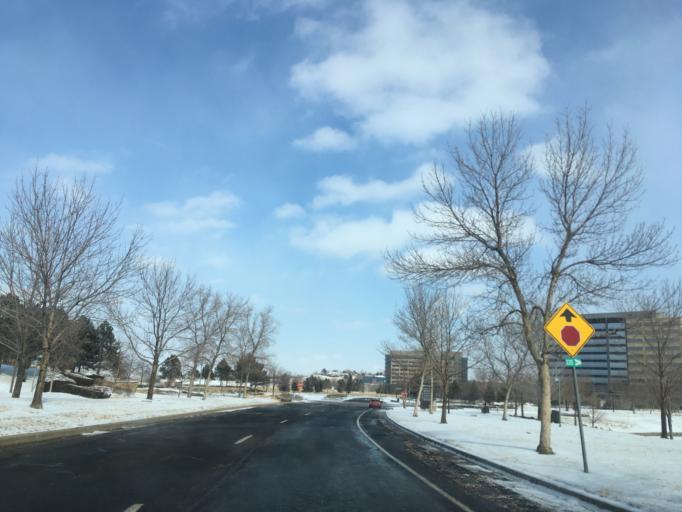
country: US
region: Colorado
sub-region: Broomfield County
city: Broomfield
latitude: 39.9231
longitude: -105.1217
